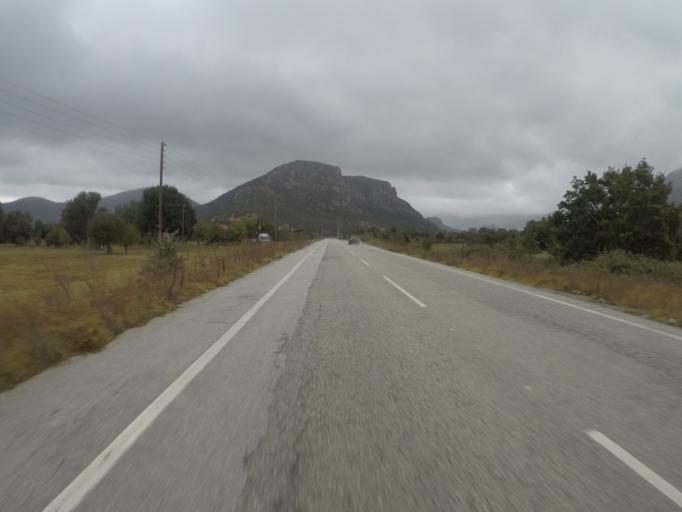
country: GR
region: Peloponnese
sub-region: Nomos Arkadias
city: Tripoli
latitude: 37.5891
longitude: 22.4270
